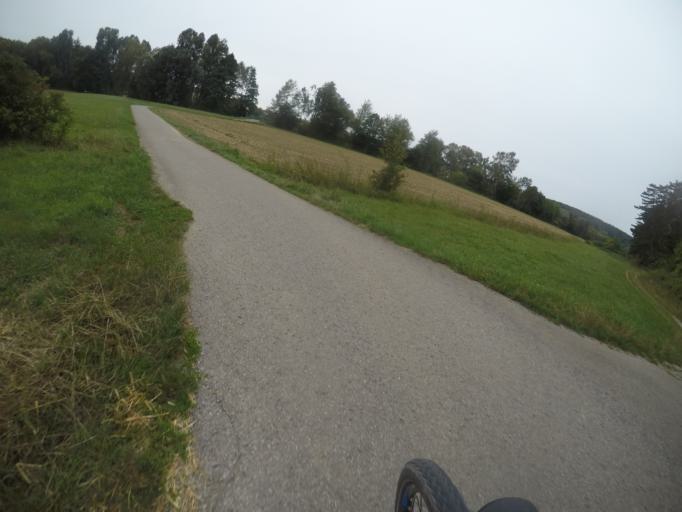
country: DE
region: Baden-Wuerttemberg
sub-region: Regierungsbezirk Stuttgart
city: Weil der Stadt
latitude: 48.7637
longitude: 8.8764
